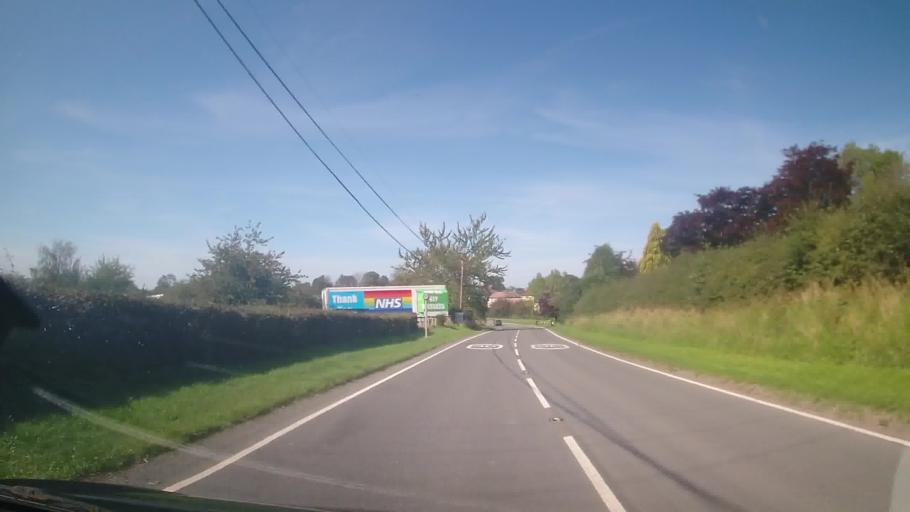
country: GB
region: England
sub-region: Shropshire
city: Mainstone
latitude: 52.5355
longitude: -3.0606
